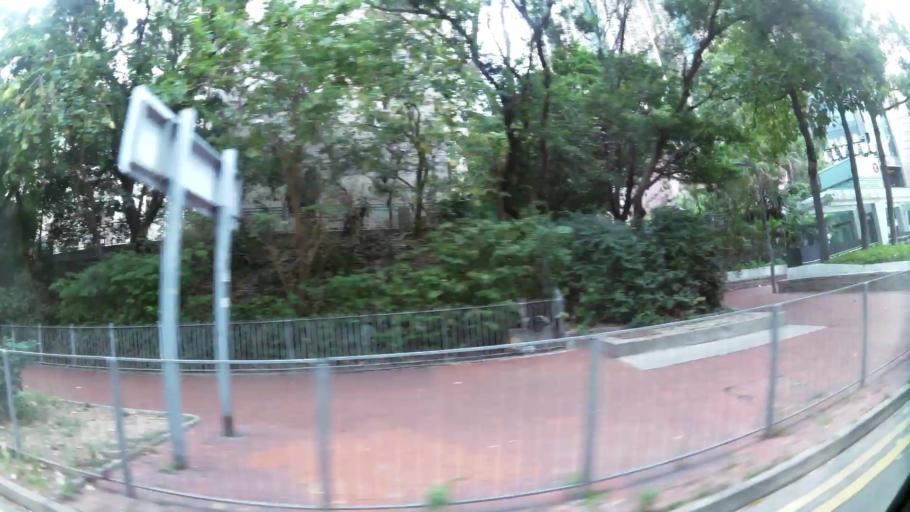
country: HK
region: Wong Tai Sin
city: Wong Tai Sin
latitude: 22.3408
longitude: 114.2006
